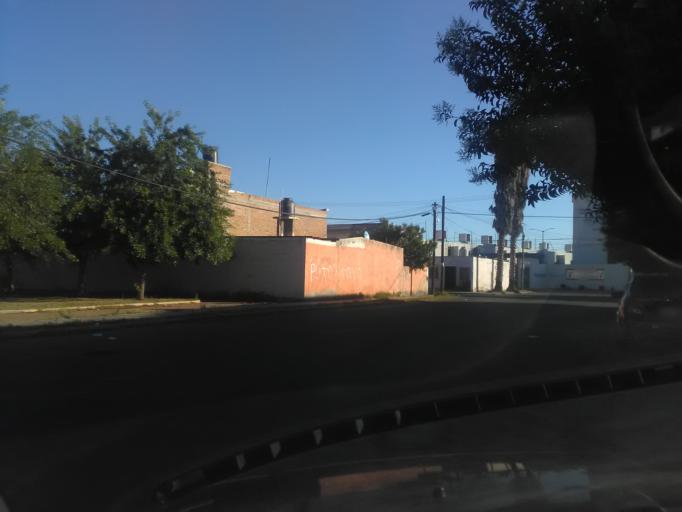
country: MX
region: Durango
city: Victoria de Durango
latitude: 23.9993
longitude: -104.7032
